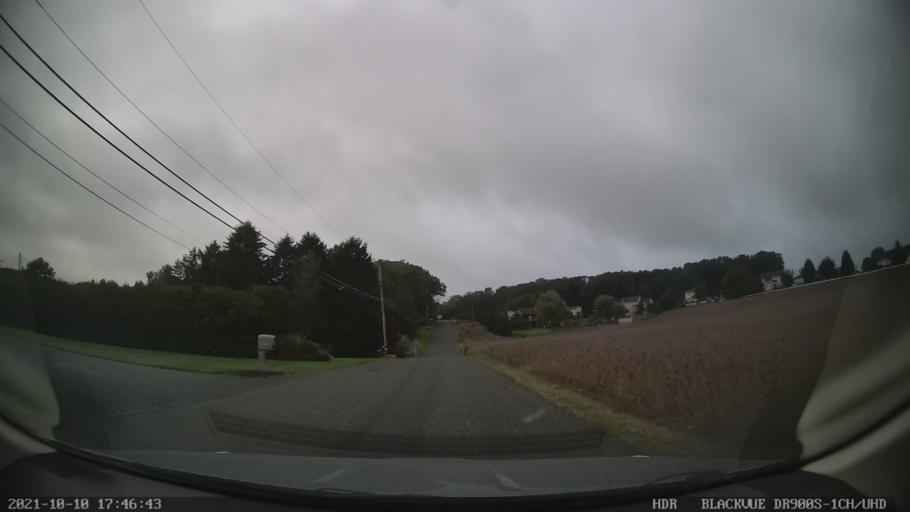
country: US
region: Pennsylvania
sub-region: Lehigh County
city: Breinigsville
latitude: 40.5674
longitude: -75.6748
